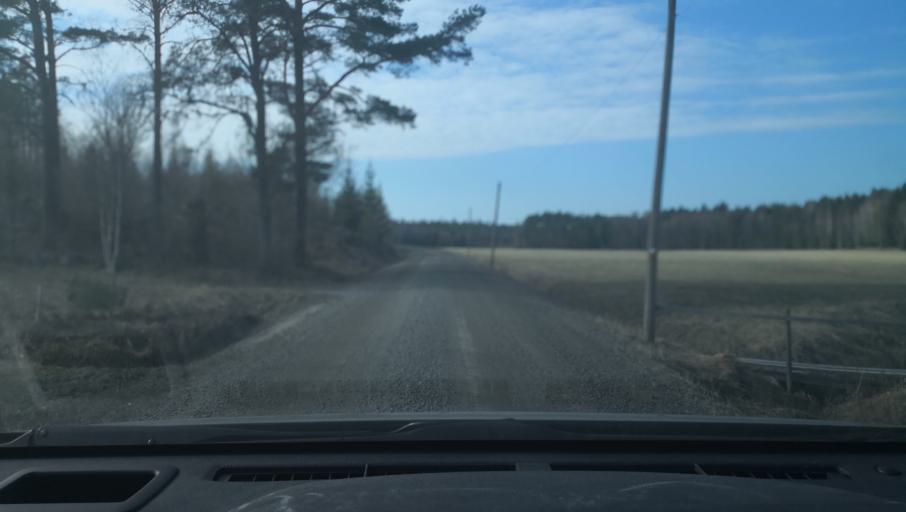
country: SE
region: Uppsala
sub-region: Heby Kommun
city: Heby
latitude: 59.8474
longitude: 16.8922
